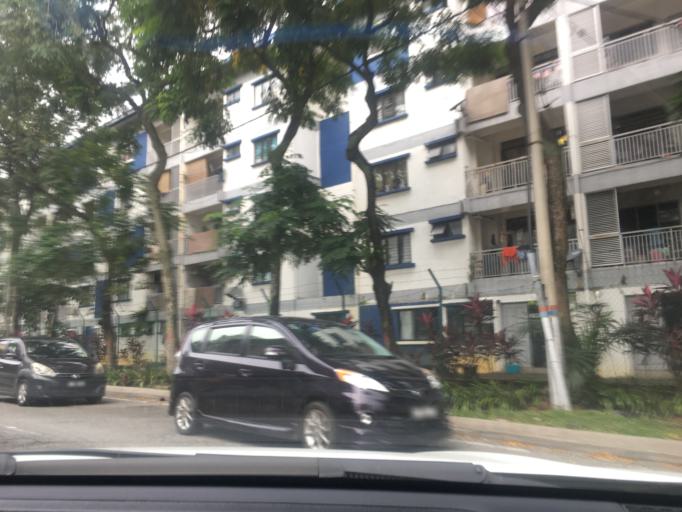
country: MY
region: Selangor
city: Klang
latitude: 3.0436
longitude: 101.4469
